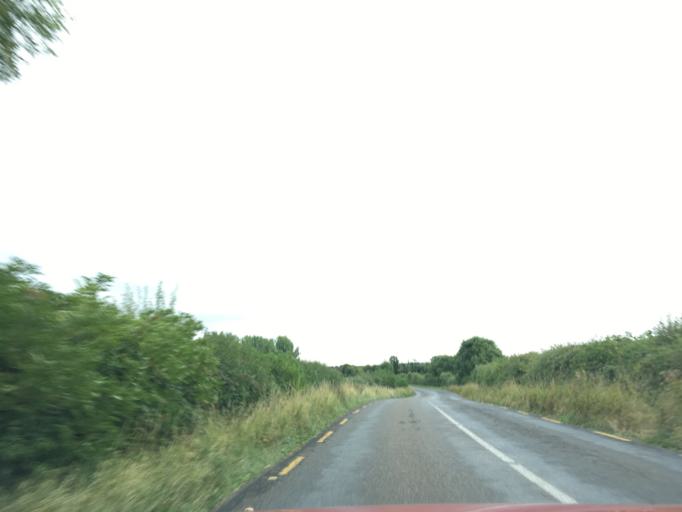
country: IE
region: Munster
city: Cashel
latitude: 52.4504
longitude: -7.8118
